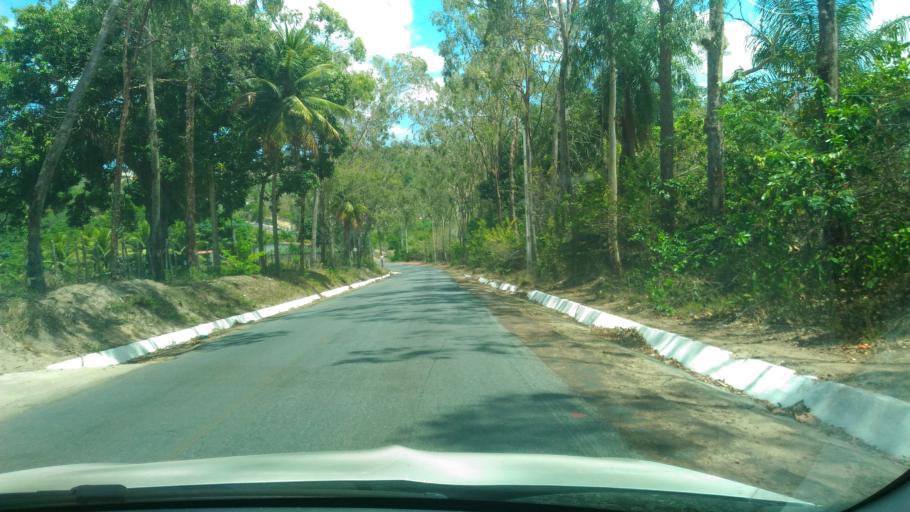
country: BR
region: Paraiba
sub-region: Conde
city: Conde
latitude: -7.2629
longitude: -34.9265
